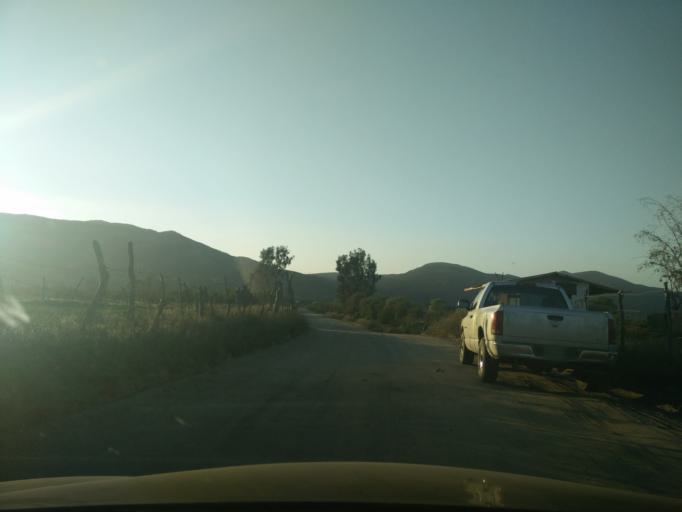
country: MX
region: Baja California
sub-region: Ensenada
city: Rancho Verde
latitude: 32.0532
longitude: -116.6445
